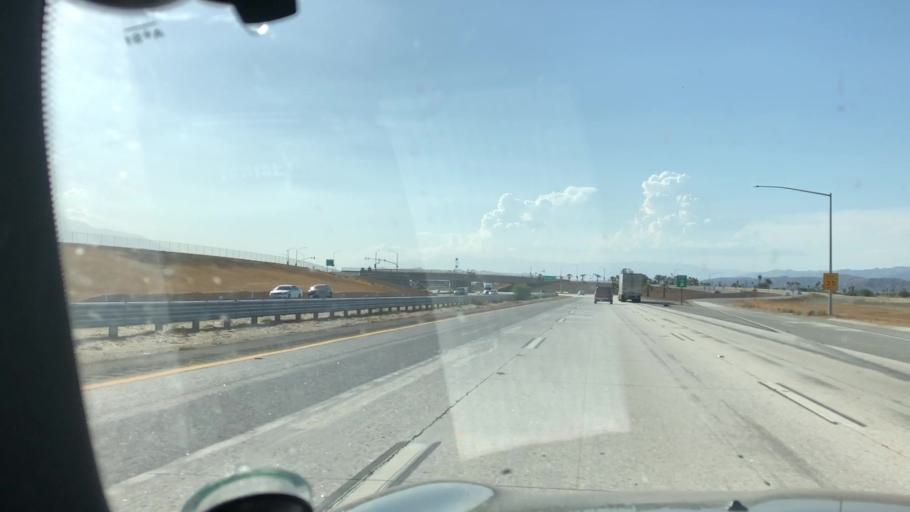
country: US
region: California
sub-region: Riverside County
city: Bermuda Dunes
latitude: 33.7465
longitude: -116.2642
